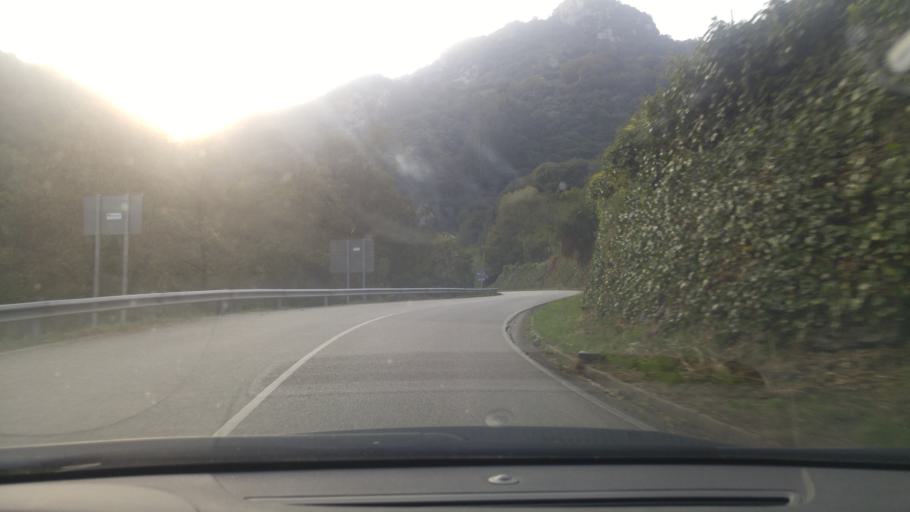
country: ES
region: Asturias
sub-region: Province of Asturias
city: Proaza
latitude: 43.2497
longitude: -6.0198
